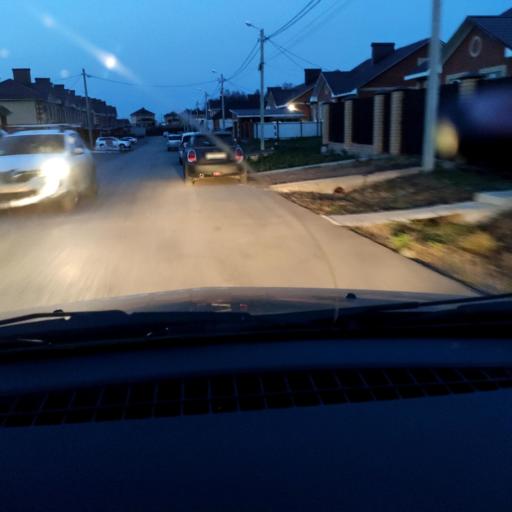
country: RU
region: Bashkortostan
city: Mikhaylovka
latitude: 54.8320
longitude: 55.8686
